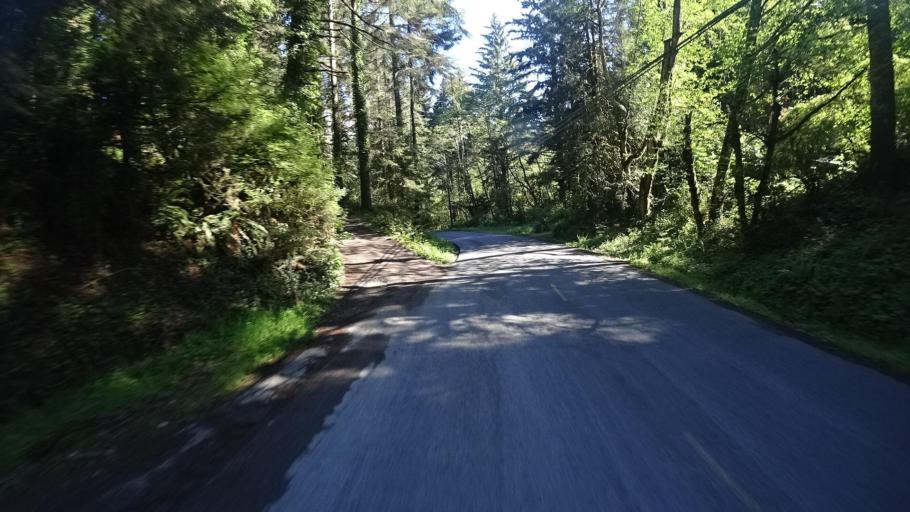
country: US
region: California
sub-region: Humboldt County
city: McKinleyville
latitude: 40.9825
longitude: -124.0984
